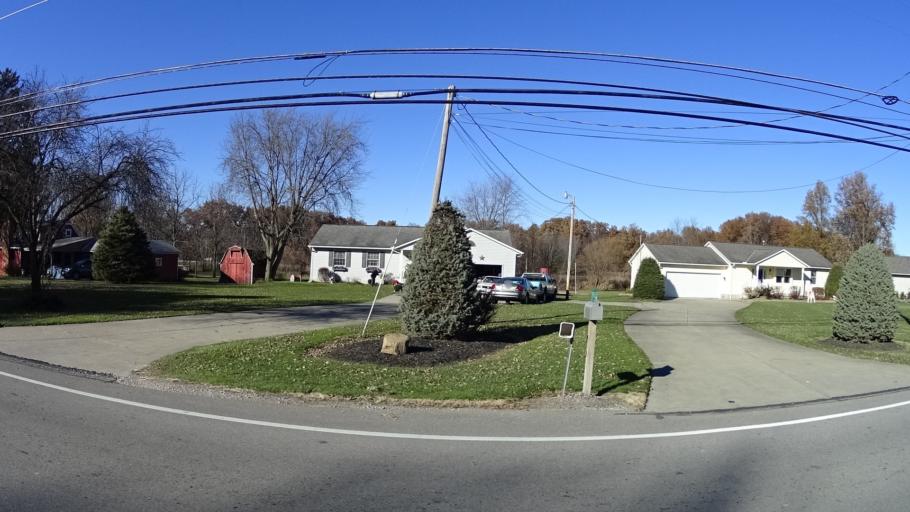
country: US
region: Ohio
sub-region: Lorain County
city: Elyria
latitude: 41.3221
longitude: -82.0958
